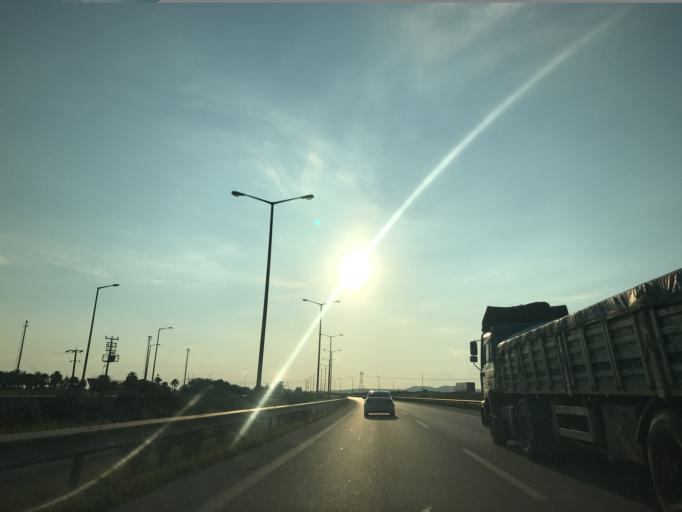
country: TR
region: Osmaniye
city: Toprakkale
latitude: 36.9720
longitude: 36.0608
